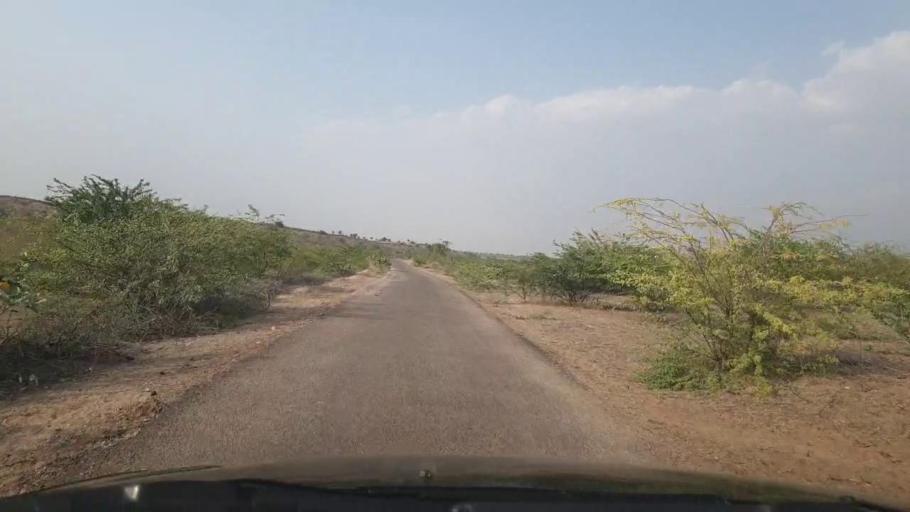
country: PK
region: Sindh
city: Islamkot
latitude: 25.0694
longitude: 70.5657
